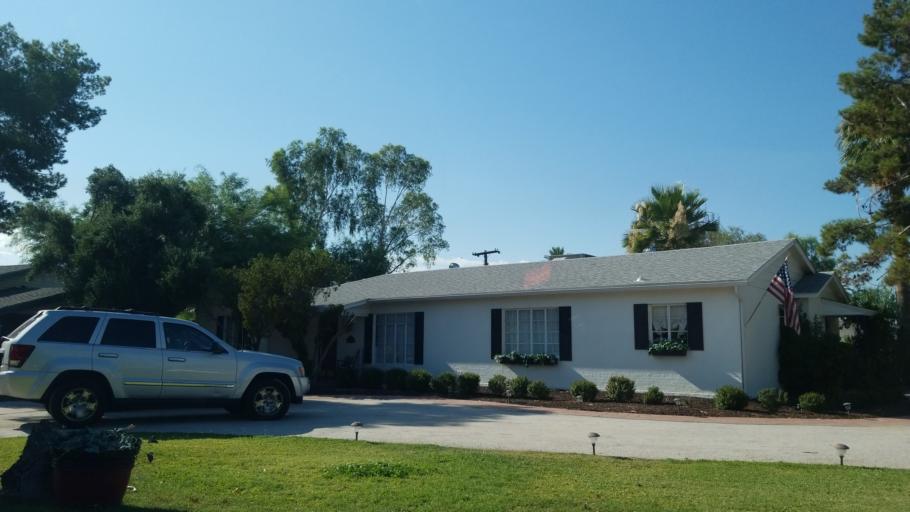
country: US
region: Arizona
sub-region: Maricopa County
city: Phoenix
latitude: 33.4794
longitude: -112.0638
